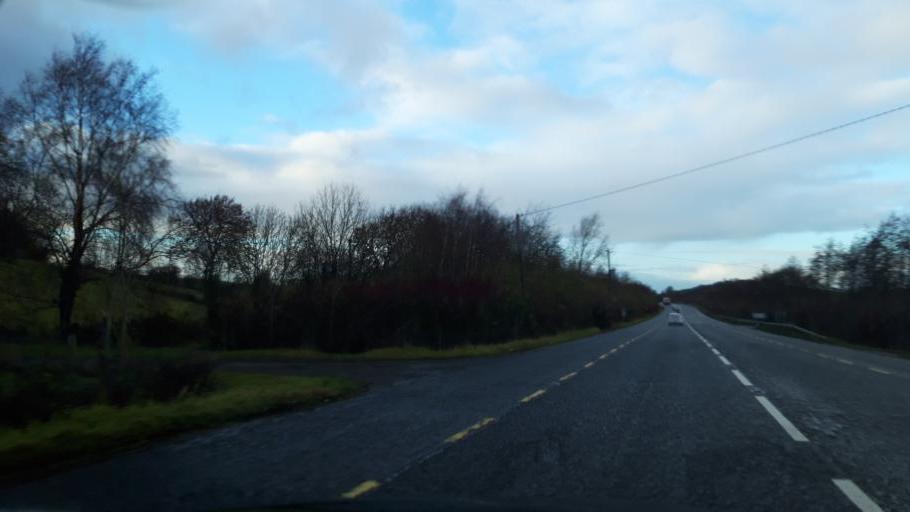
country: IE
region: Ulster
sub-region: County Monaghan
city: Carrickmacross
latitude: 53.9189
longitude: -6.6298
